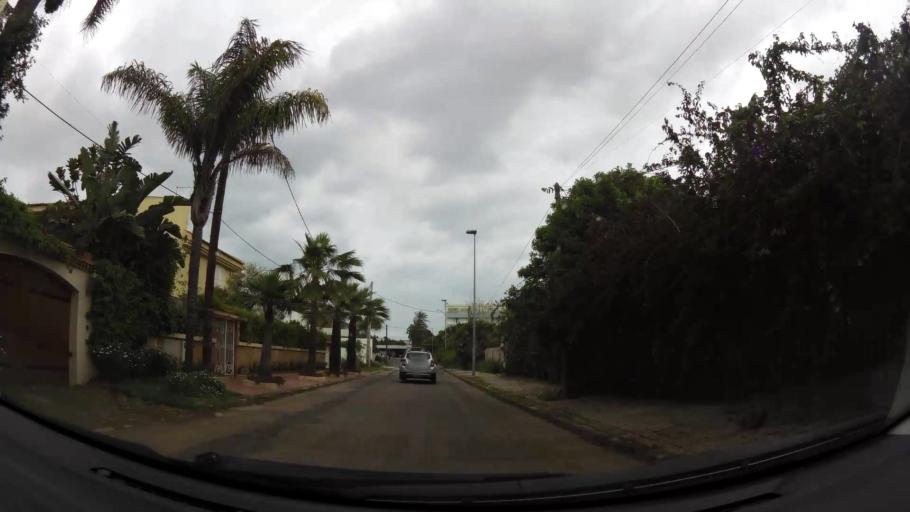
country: MA
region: Grand Casablanca
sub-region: Casablanca
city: Casablanca
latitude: 33.5937
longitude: -7.6584
